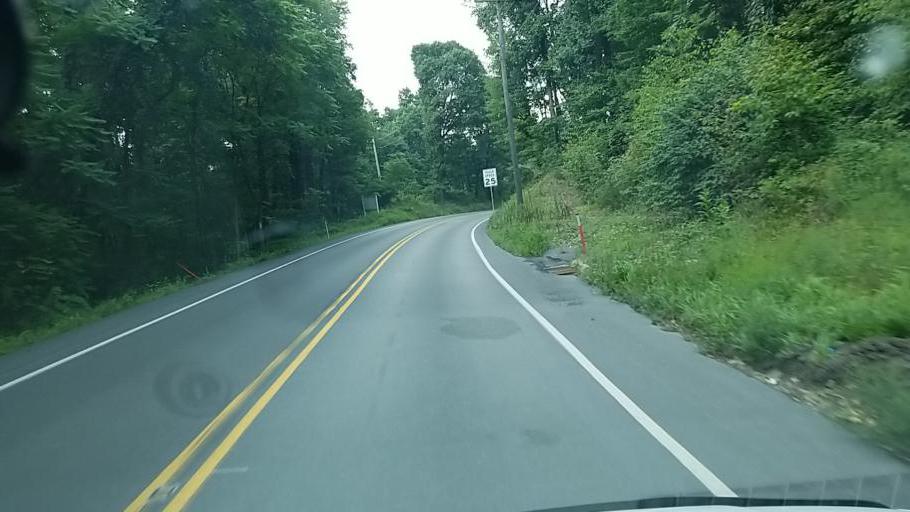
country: US
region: Pennsylvania
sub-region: Dauphin County
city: Elizabethville
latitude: 40.5348
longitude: -76.8192
